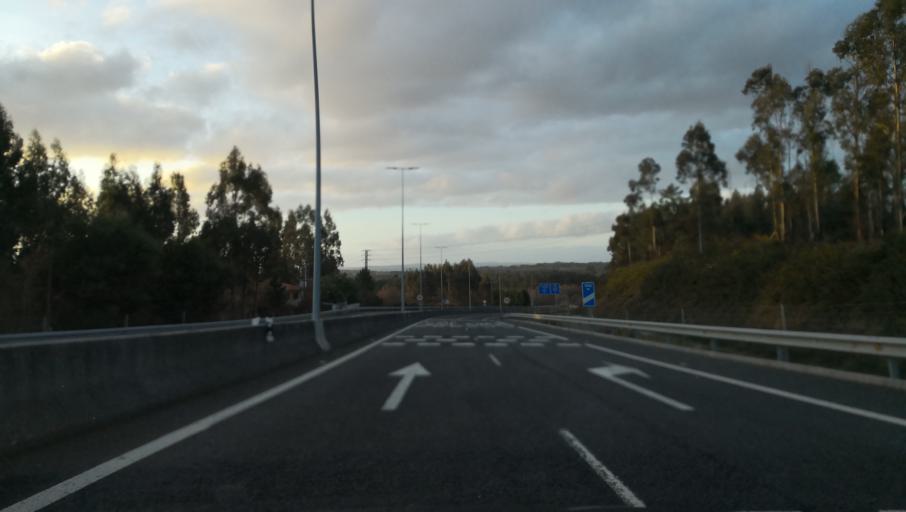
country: ES
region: Galicia
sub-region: Provincia da Coruna
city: Oroso
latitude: 42.9066
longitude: -8.4303
